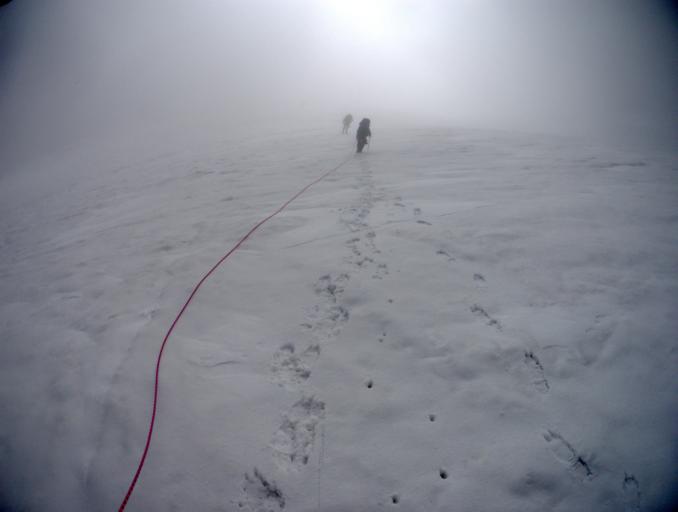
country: RU
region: Kabardino-Balkariya
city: Terskol
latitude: 43.3833
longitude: 42.4369
